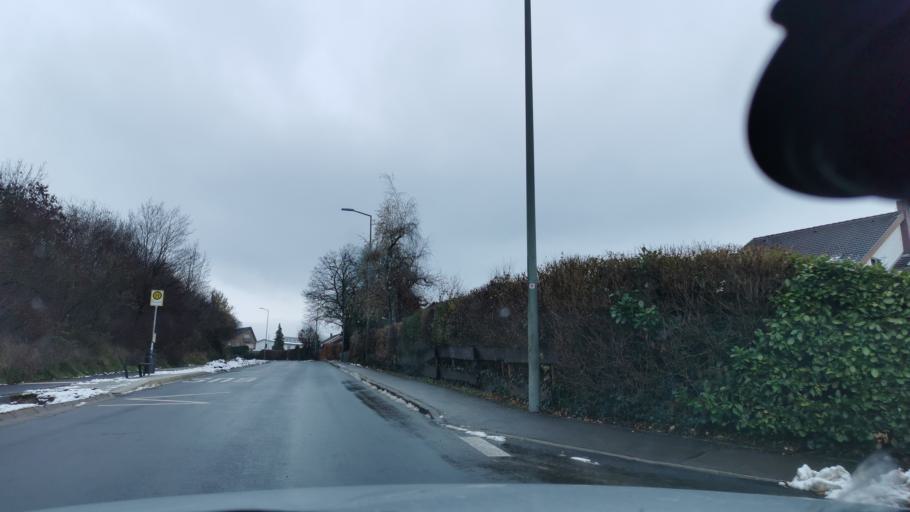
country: DE
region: Baden-Wuerttemberg
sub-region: Regierungsbezirk Stuttgart
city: Eislingen
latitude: 48.7054
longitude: 9.7137
